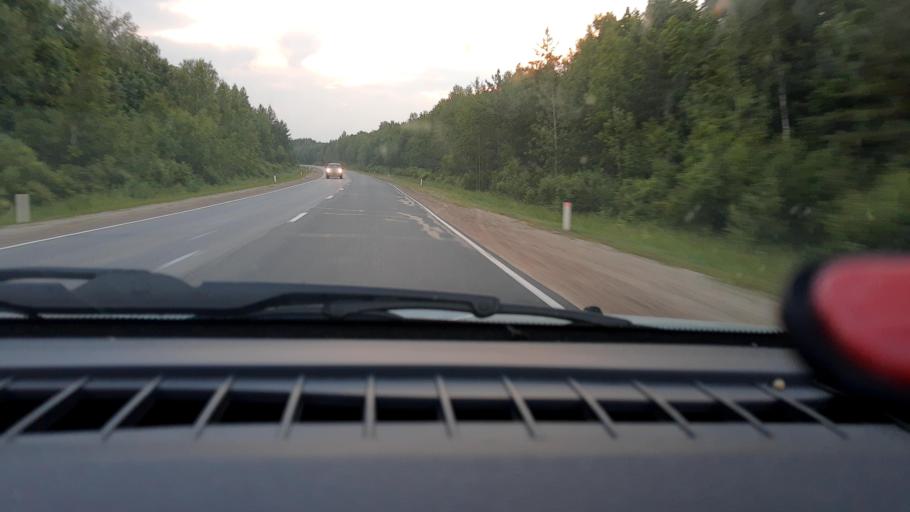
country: RU
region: Nizjnij Novgorod
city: Arzamas
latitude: 55.4134
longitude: 43.9145
